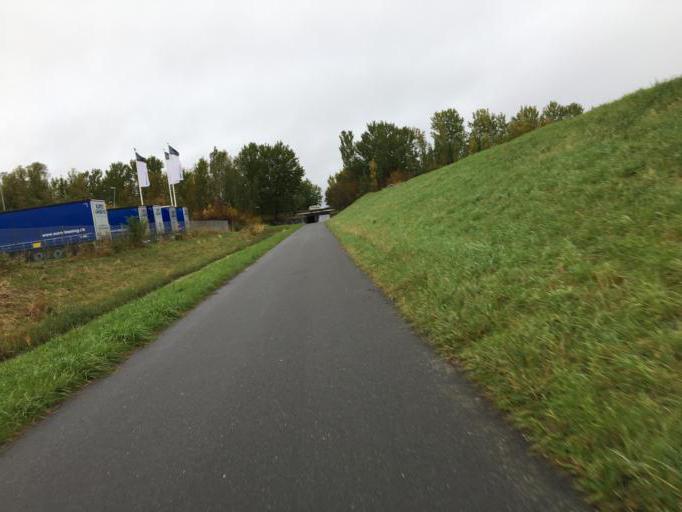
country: DK
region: Capital Region
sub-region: Hvidovre Kommune
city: Hvidovre
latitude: 55.6137
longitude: 12.4970
